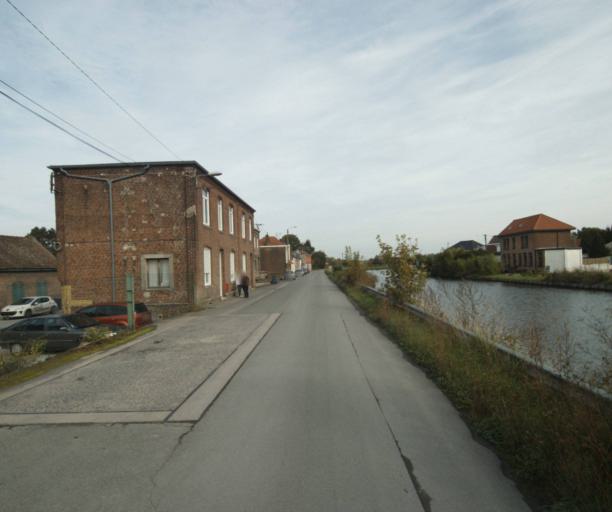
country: FR
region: Nord-Pas-de-Calais
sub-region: Departement du Nord
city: Don
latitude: 50.5485
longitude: 2.9118
